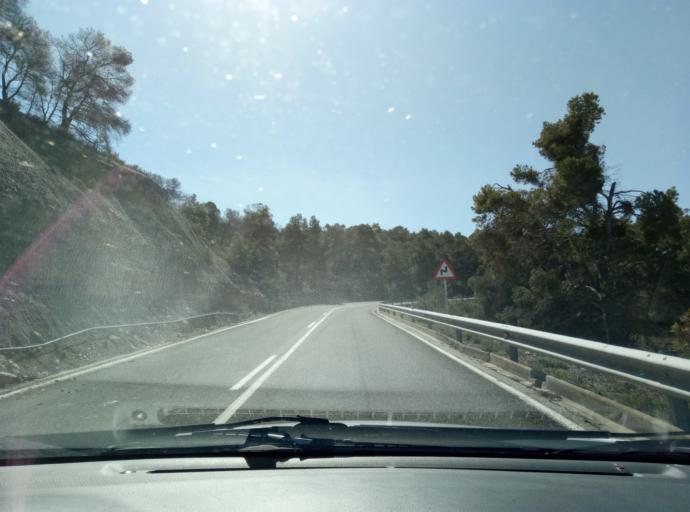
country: ES
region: Catalonia
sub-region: Provincia de Lleida
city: Vallbona de les Monges
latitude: 41.5304
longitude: 1.0261
